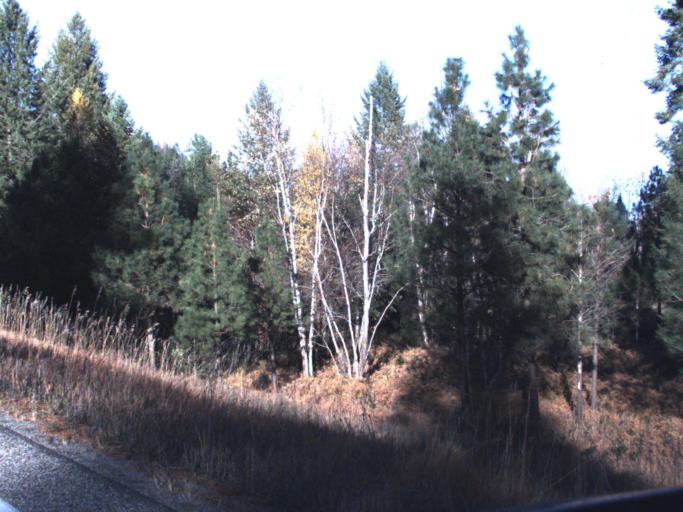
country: CA
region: British Columbia
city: Rossland
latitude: 48.9436
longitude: -117.7719
